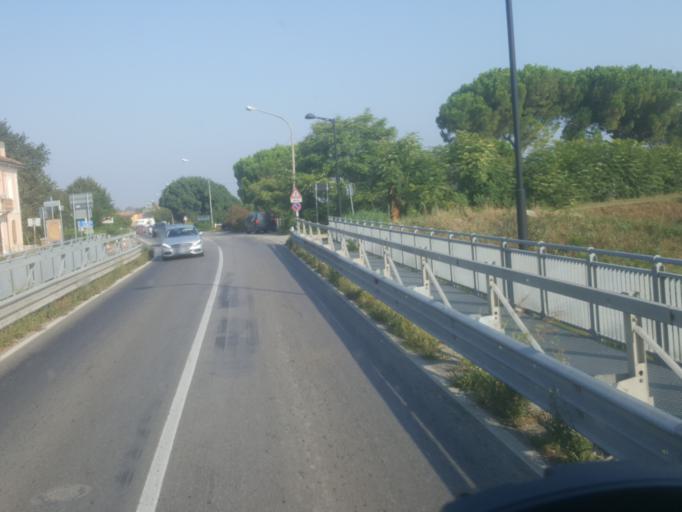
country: IT
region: Emilia-Romagna
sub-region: Provincia di Ravenna
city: Mezzano
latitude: 44.4697
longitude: 12.0829
